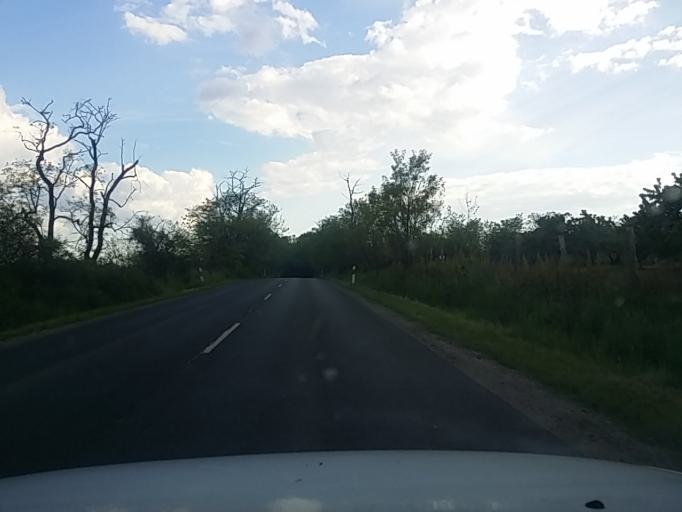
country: HU
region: Pest
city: Mogyorod
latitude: 47.6450
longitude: 19.2330
